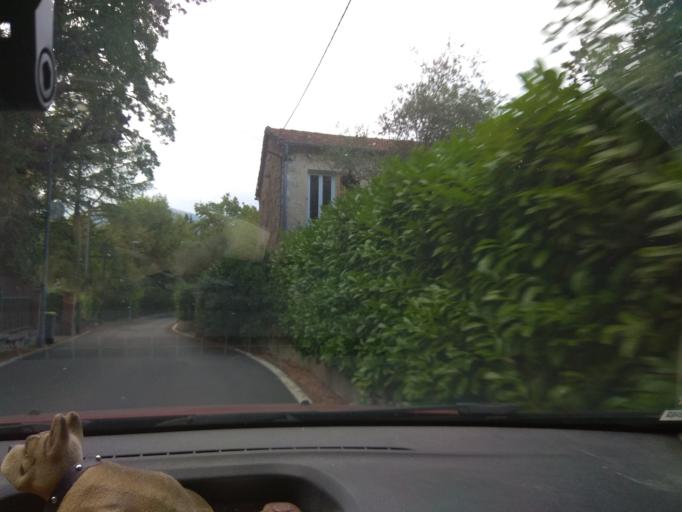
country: FR
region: Provence-Alpes-Cote d'Azur
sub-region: Departement des Alpes-Maritimes
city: Le Rouret
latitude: 43.6734
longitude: 7.0462
